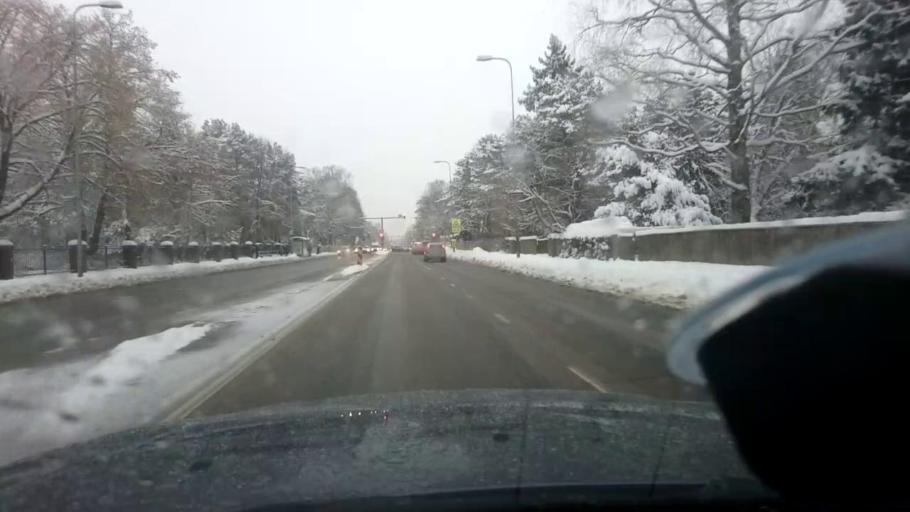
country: EE
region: Harju
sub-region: Tallinna linn
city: Tallinn
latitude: 59.3822
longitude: 24.7033
